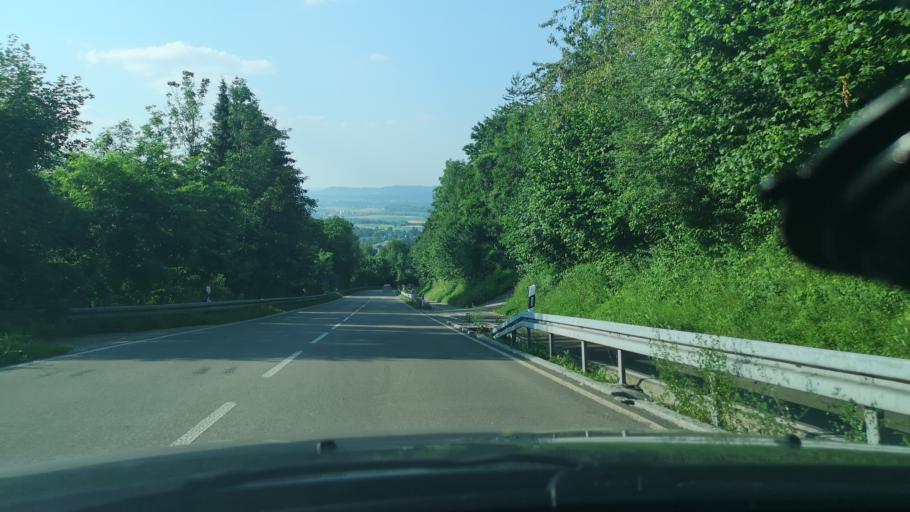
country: DE
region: Baden-Wuerttemberg
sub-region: Regierungsbezirk Stuttgart
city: Schlat
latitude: 48.6389
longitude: 9.7025
